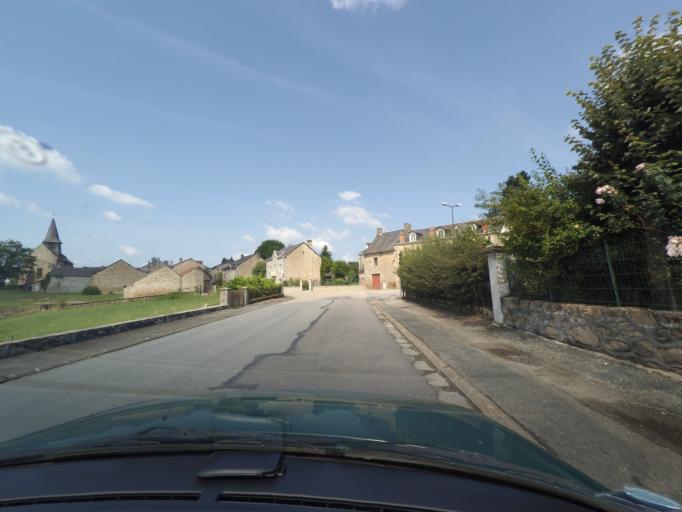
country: FR
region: Limousin
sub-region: Departement de la Haute-Vienne
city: Eymoutiers
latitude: 45.7193
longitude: 1.8332
